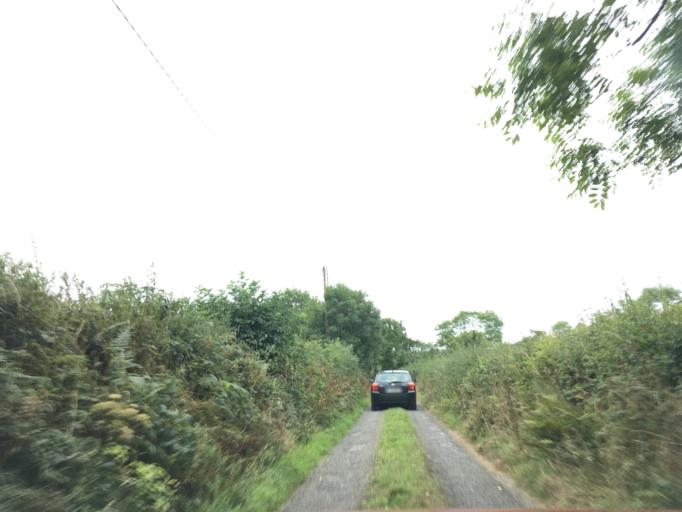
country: IE
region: Munster
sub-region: An Clar
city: Ennis
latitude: 52.7227
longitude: -9.0967
